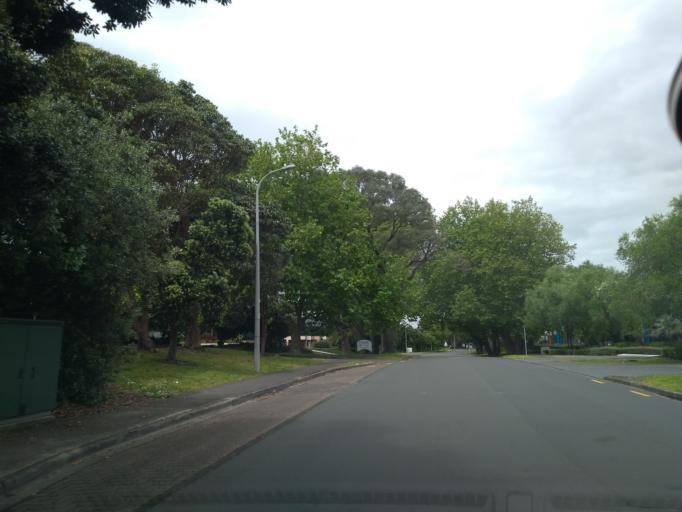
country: NZ
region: Auckland
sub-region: Auckland
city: Tamaki
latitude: -36.9219
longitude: 174.8217
